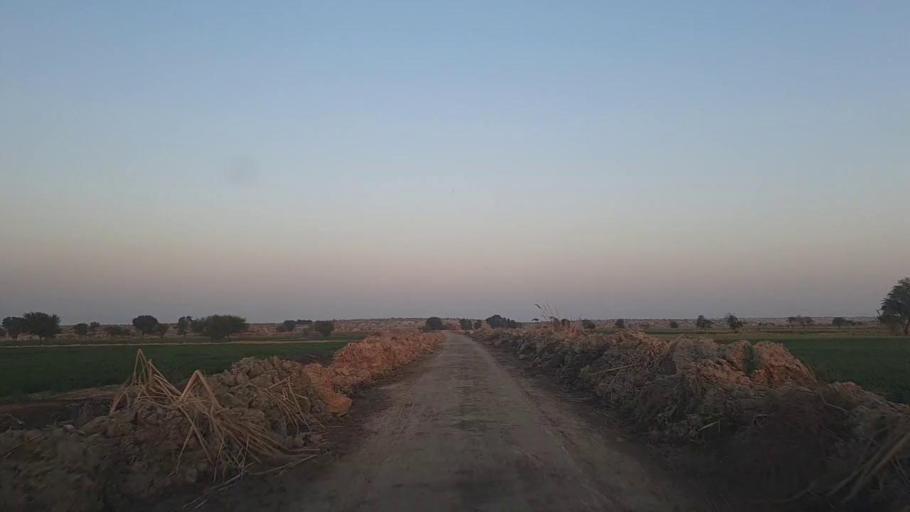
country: PK
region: Sindh
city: Jam Sahib
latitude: 26.3877
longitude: 68.6970
